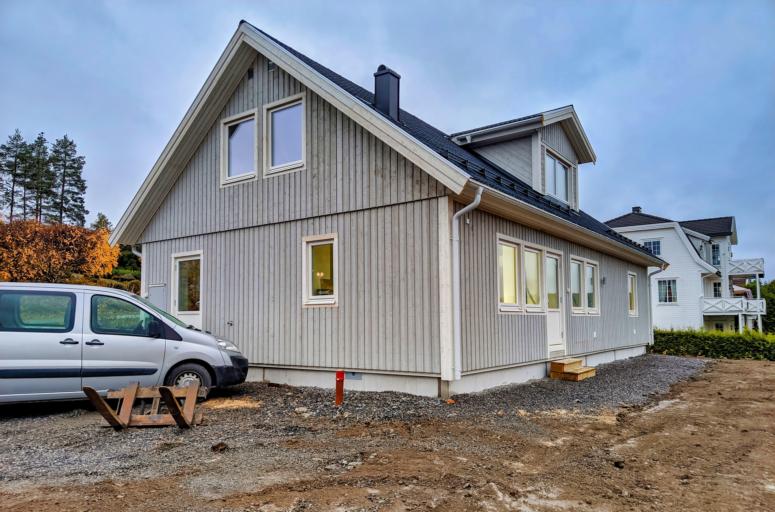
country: NO
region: Hedmark
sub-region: Sor-Odal
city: Skarnes
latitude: 60.2760
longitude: 11.7733
